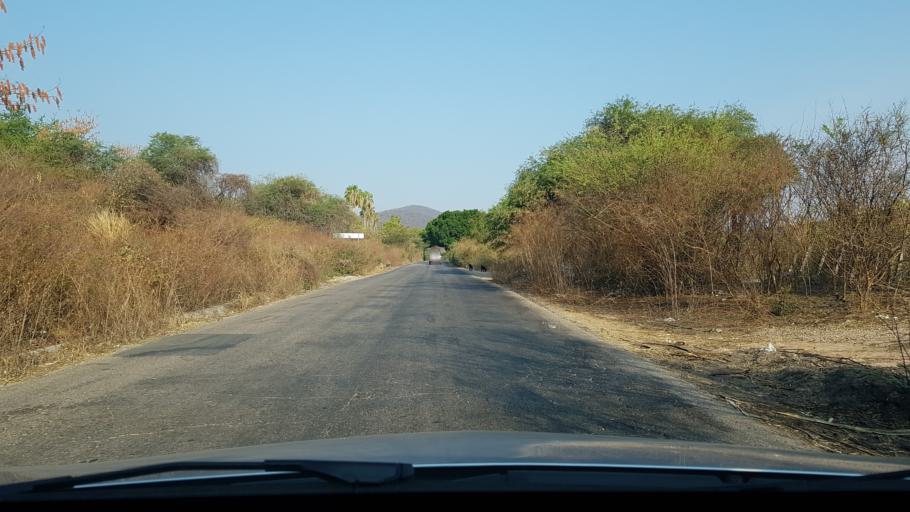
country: MX
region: Morelos
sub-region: Tepalcingo
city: Zacapalco
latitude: 18.6521
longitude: -99.0315
